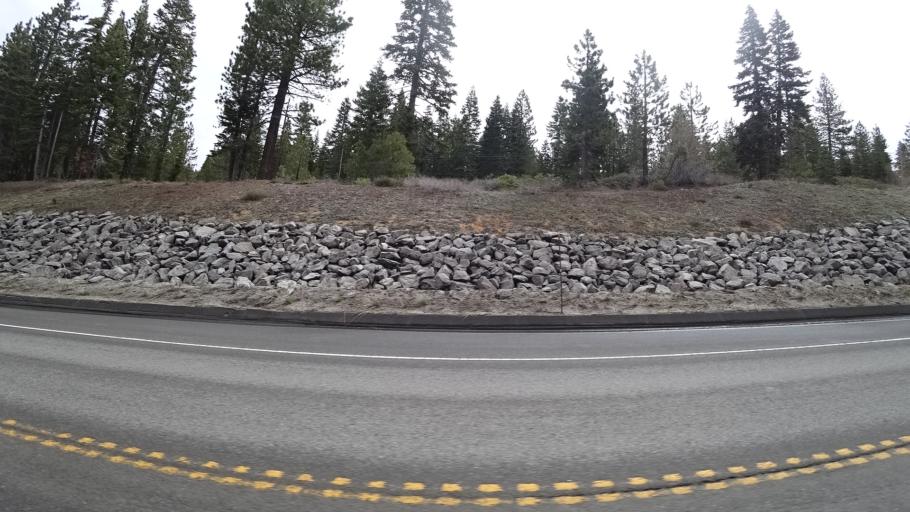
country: US
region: California
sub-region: Placer County
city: Tahoe Vista
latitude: 39.2659
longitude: -120.0723
